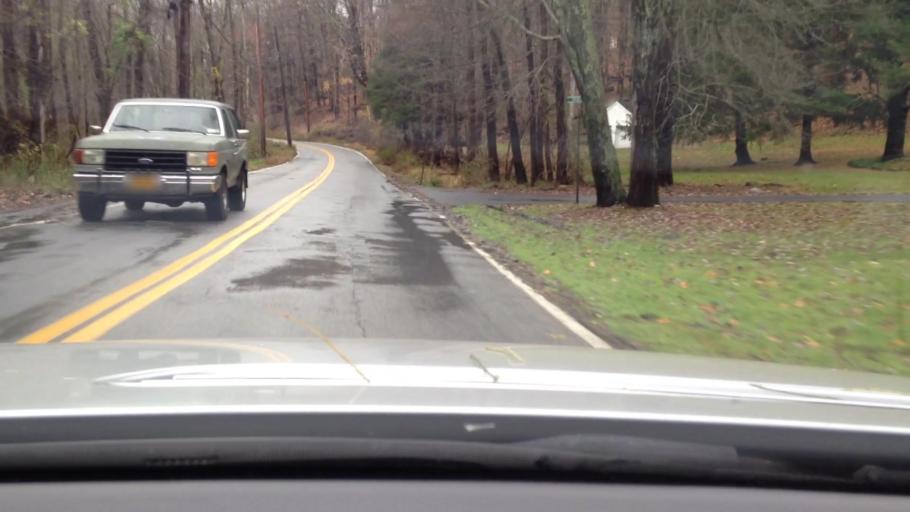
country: US
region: New York
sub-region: Westchester County
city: Croton-on-Hudson
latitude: 41.2354
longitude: -73.8921
